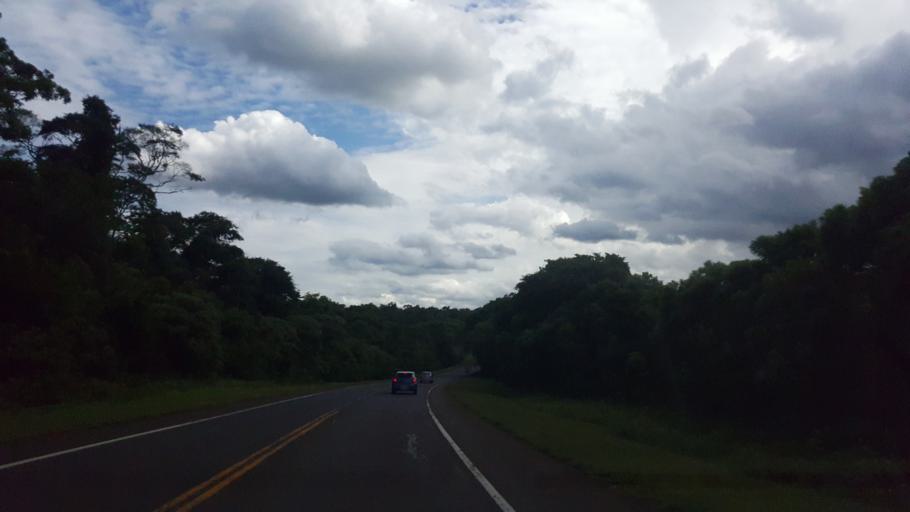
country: AR
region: Misiones
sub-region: Departamento de Iguazu
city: Puerto Iguazu
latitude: -25.7035
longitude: -54.5149
